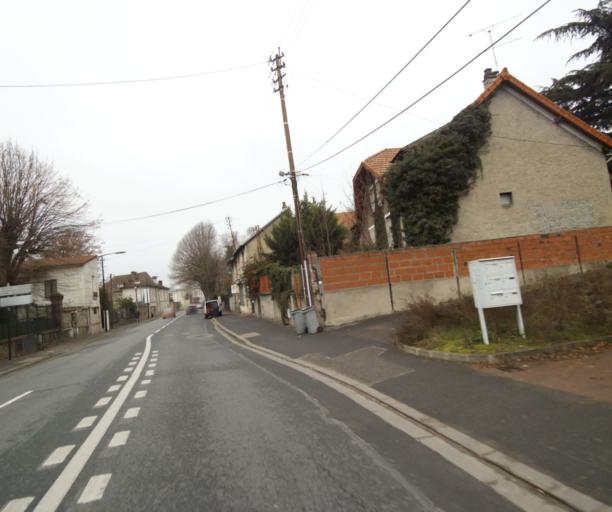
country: FR
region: Ile-de-France
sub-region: Departement des Hauts-de-Seine
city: Rueil-Malmaison
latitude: 48.8694
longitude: 2.1858
